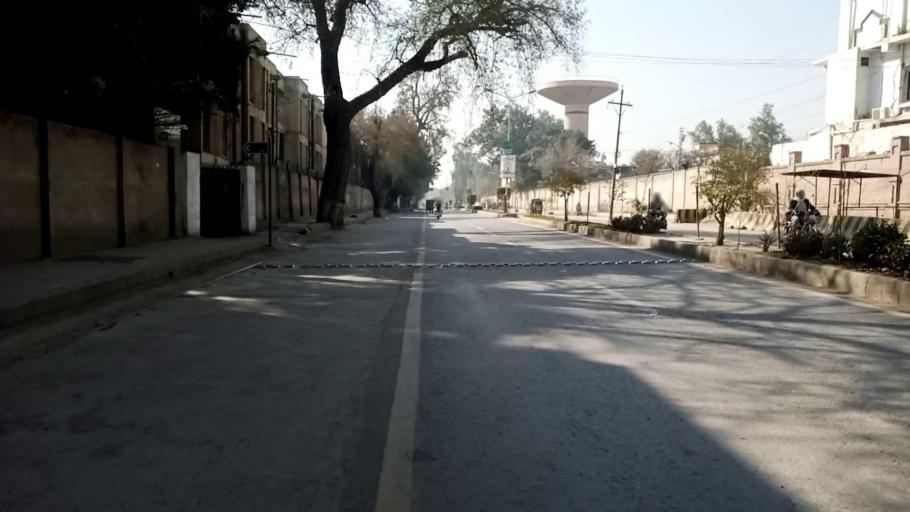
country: PK
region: Khyber Pakhtunkhwa
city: Peshawar
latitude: 33.9900
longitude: 71.5324
